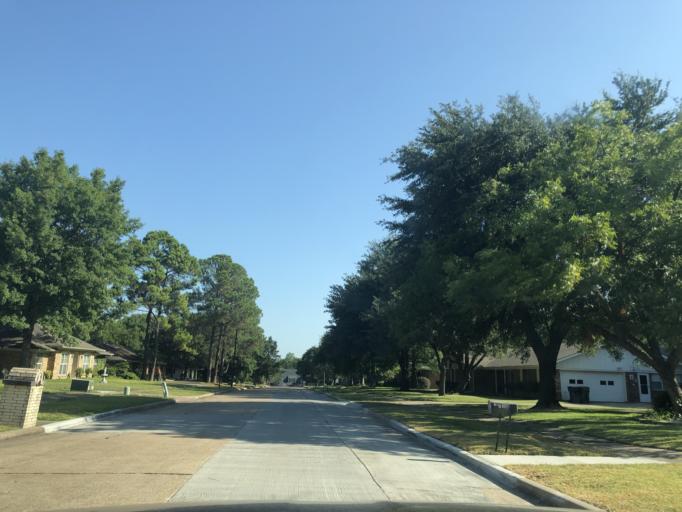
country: US
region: Texas
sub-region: Dallas County
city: Garland
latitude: 32.8688
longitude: -96.6407
